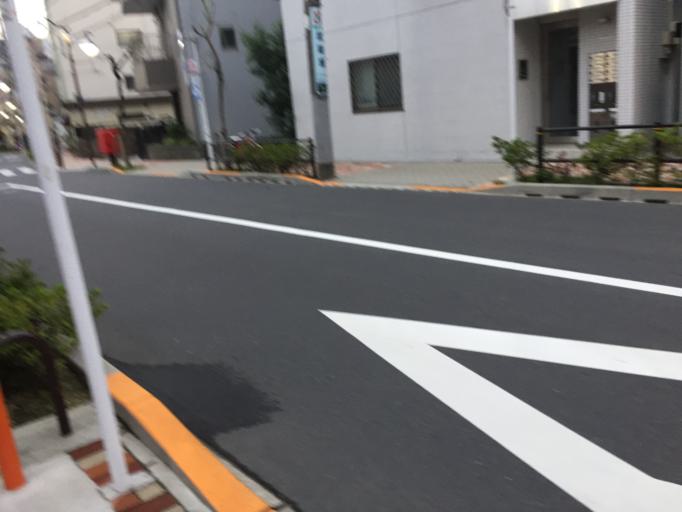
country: JP
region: Tokyo
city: Tokyo
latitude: 35.7120
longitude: 139.6691
